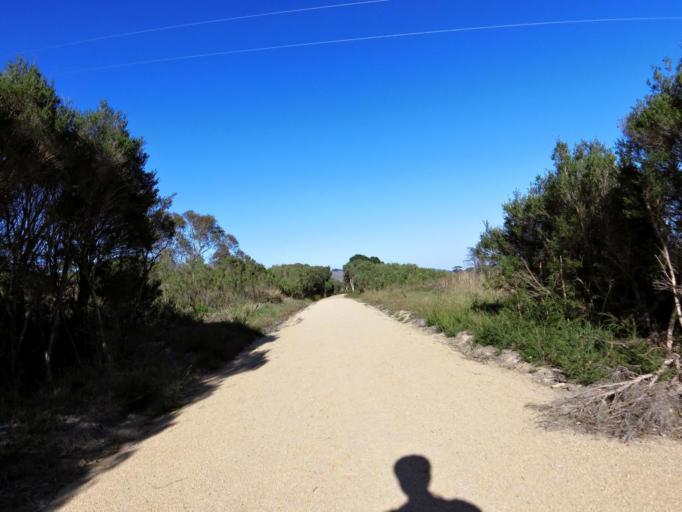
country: AU
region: Victoria
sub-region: Bass Coast
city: North Wonthaggi
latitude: -38.5014
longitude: 145.5011
